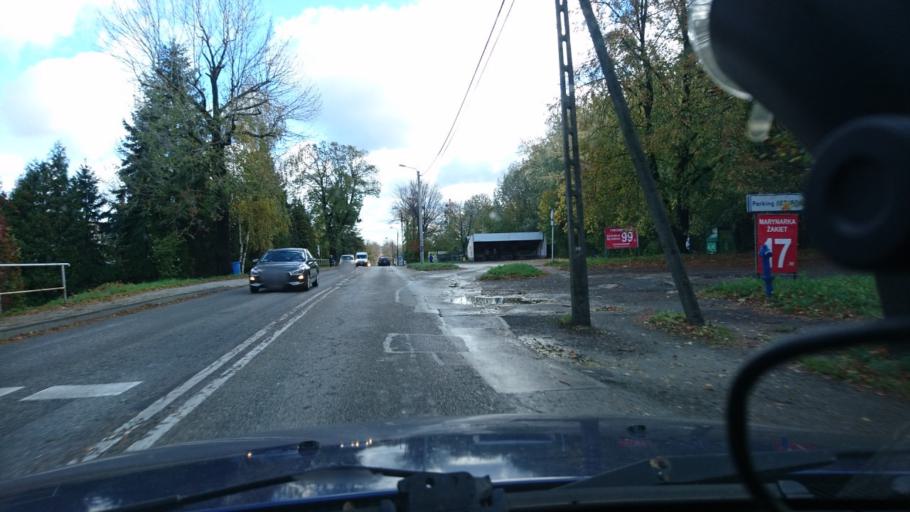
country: PL
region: Silesian Voivodeship
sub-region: Bielsko-Biala
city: Bielsko-Biala
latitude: 49.8092
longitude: 18.9977
